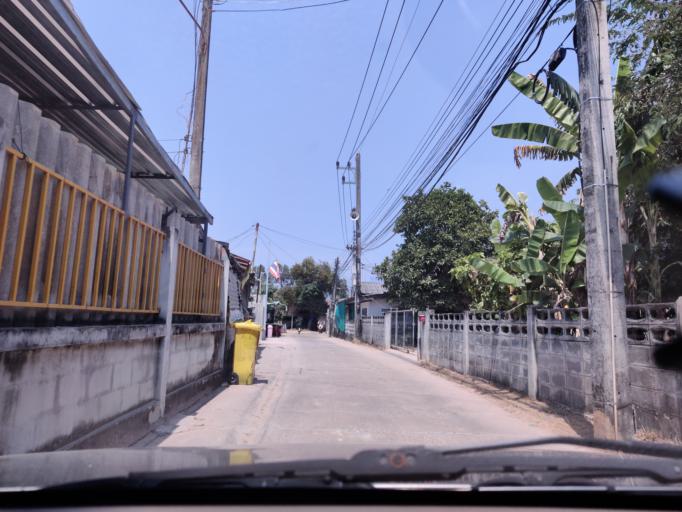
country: TH
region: Sisaket
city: Si Sa Ket
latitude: 15.1035
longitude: 104.3526
